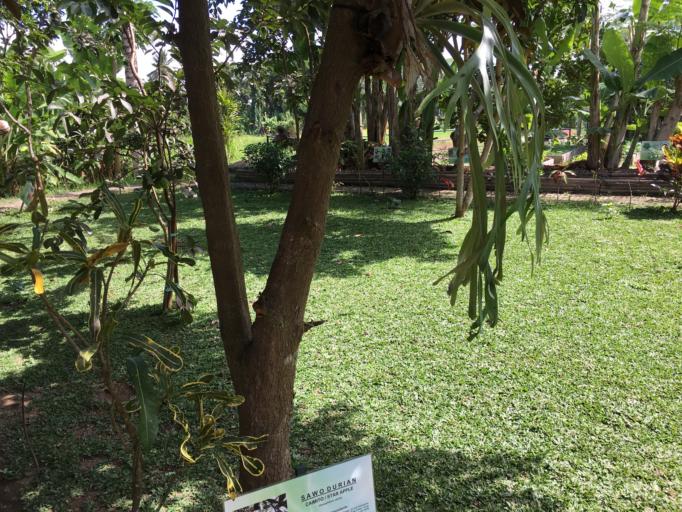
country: ID
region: Bali
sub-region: Kabupaten Gianyar
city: Ubud
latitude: -8.4951
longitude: 115.2524
